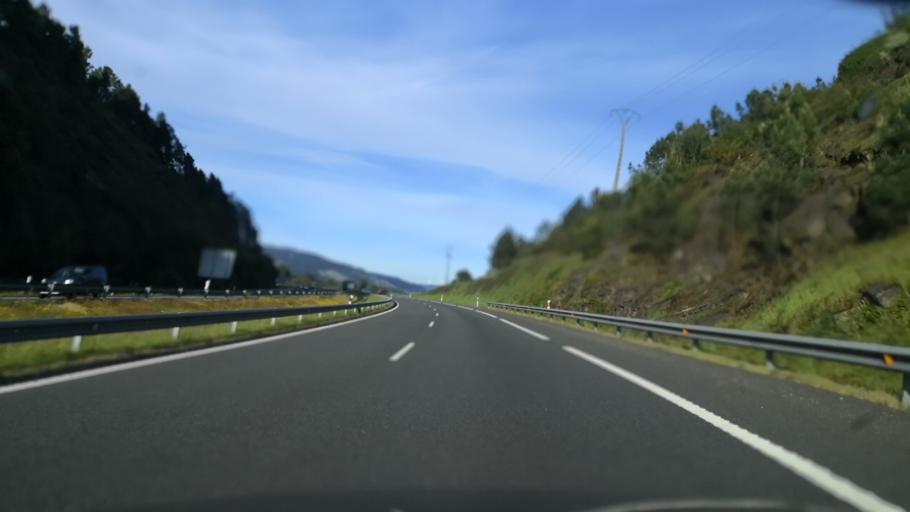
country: ES
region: Galicia
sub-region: Provincia de Ourense
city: Cenlle
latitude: 42.3081
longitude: -8.1016
